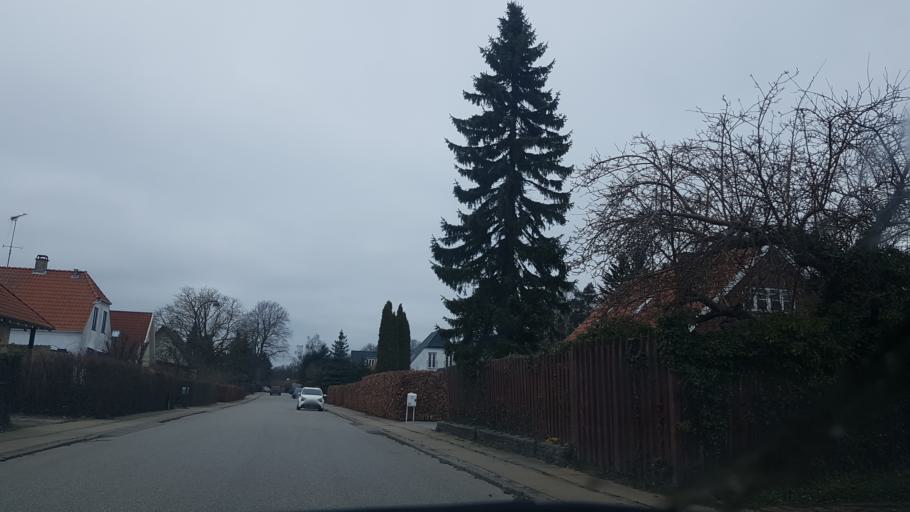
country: DK
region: Capital Region
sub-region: Lyngby-Tarbaek Kommune
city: Kongens Lyngby
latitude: 55.7507
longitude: 12.5100
